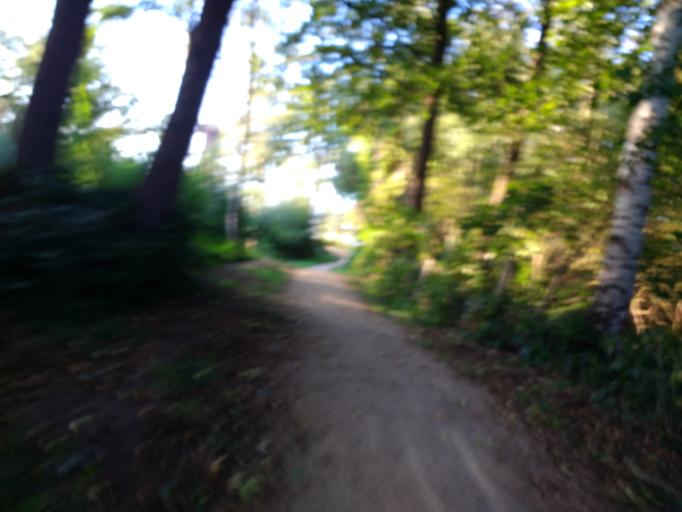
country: DE
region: Lower Saxony
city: Gifhorn
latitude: 52.4914
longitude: 10.5553
